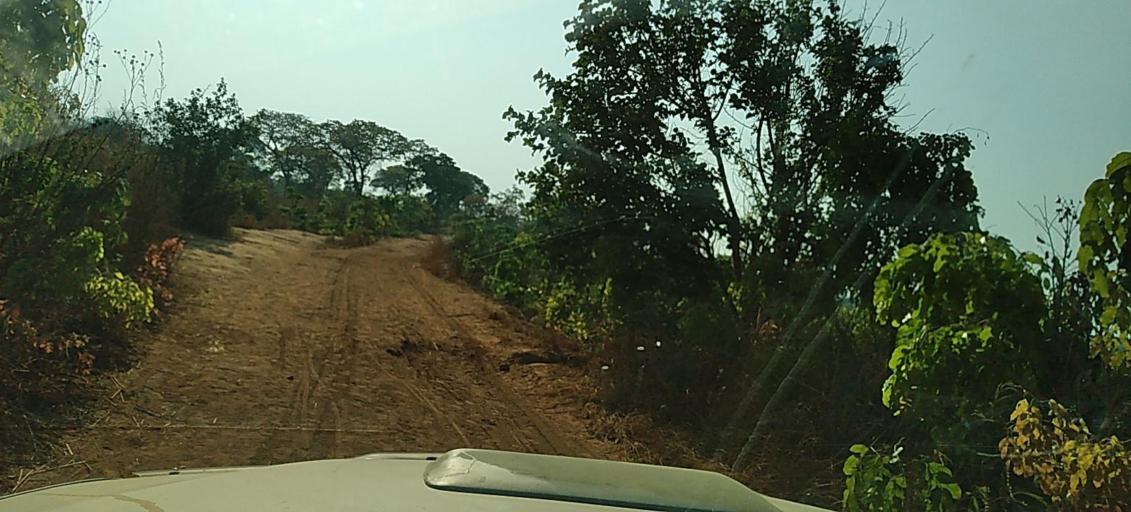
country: ZM
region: North-Western
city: Kasempa
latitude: -13.1840
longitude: 25.9528
